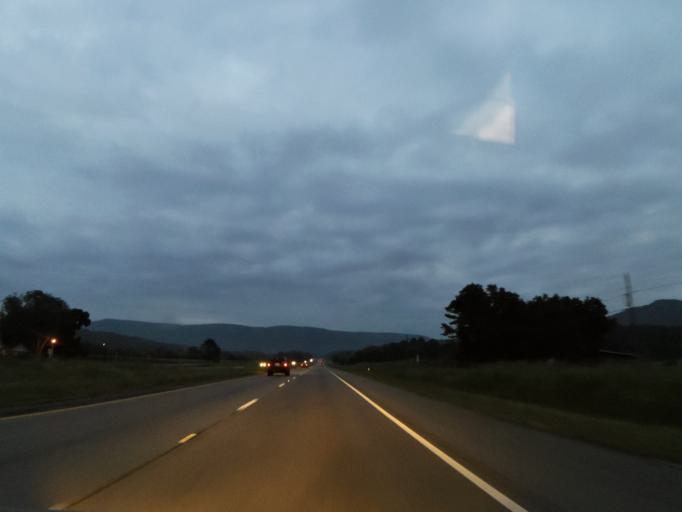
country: US
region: Alabama
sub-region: Madison County
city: Owens Cross Roads
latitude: 34.6907
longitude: -86.3529
